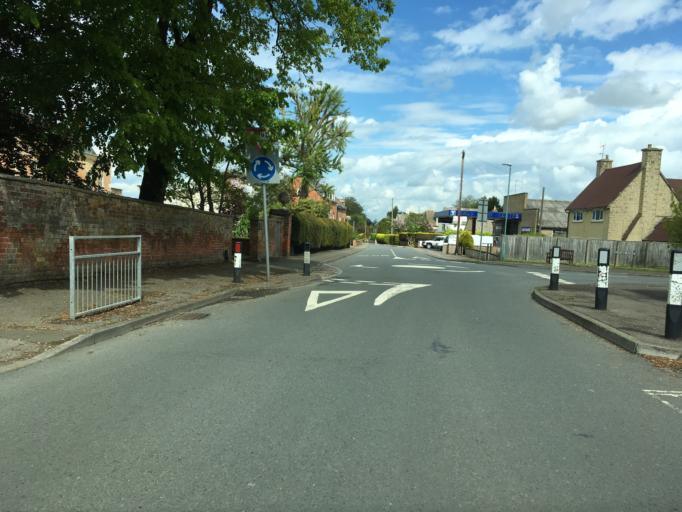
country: GB
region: England
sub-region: Gloucestershire
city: Stonehouse
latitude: 51.7321
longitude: -2.2745
